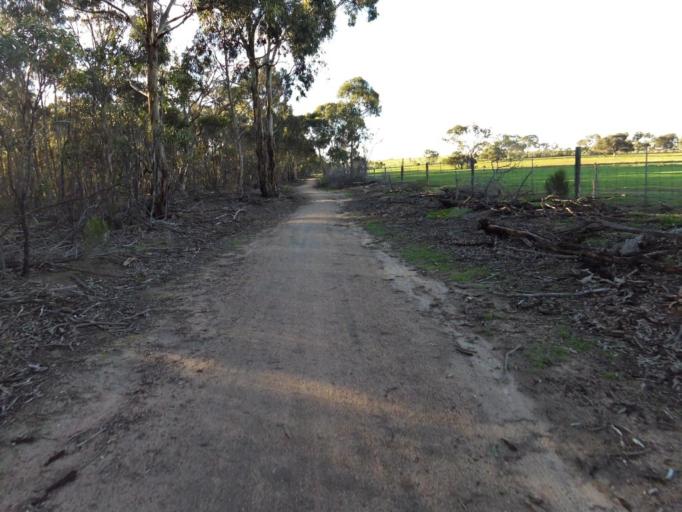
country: AU
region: Victoria
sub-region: Wyndham
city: Little River
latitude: -37.9570
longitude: 144.4453
